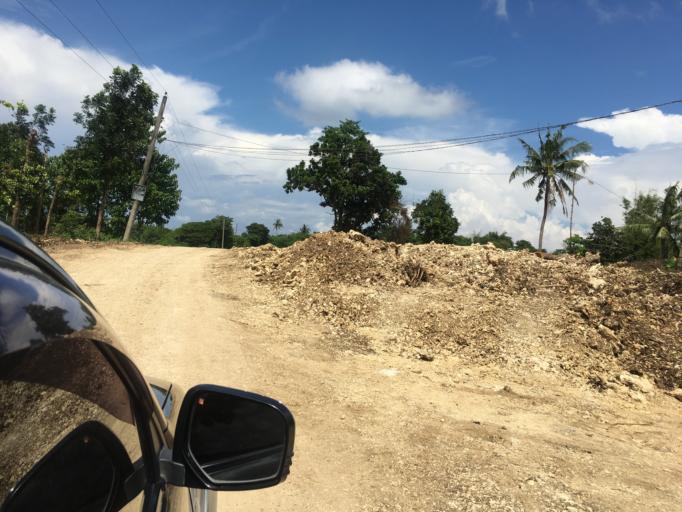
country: PH
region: Ilocos
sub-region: Province of Pangasinan
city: Catuday
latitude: 16.2632
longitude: 119.7990
